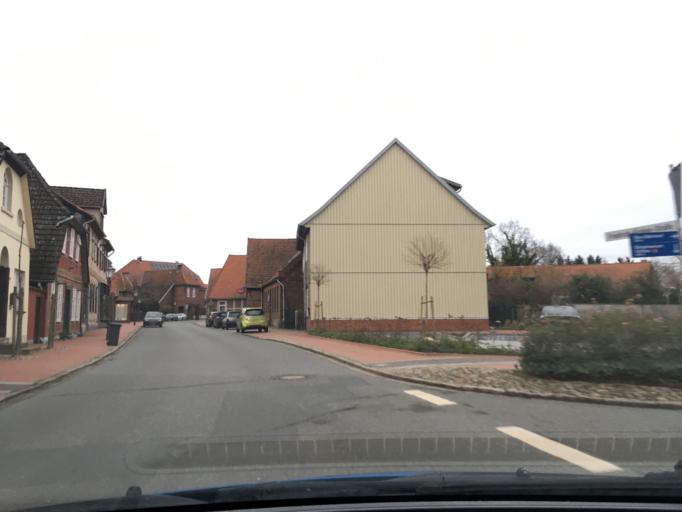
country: DE
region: Lower Saxony
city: Bleckede
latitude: 53.2935
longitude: 10.7274
